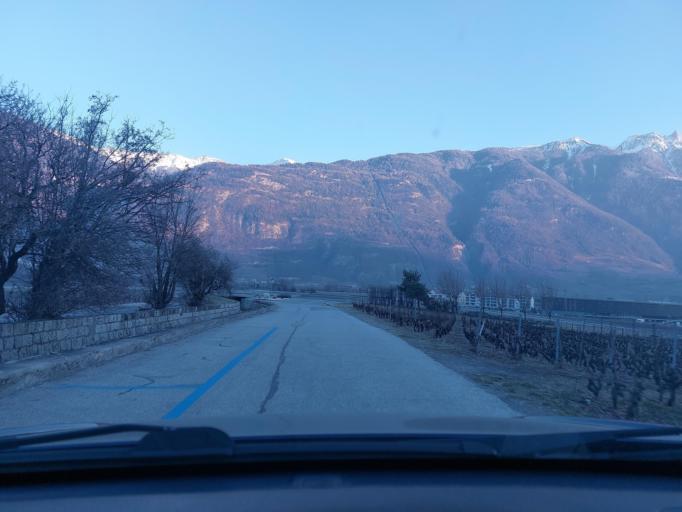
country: CH
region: Valais
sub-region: Martigny District
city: Saillon
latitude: 46.1784
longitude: 7.1950
